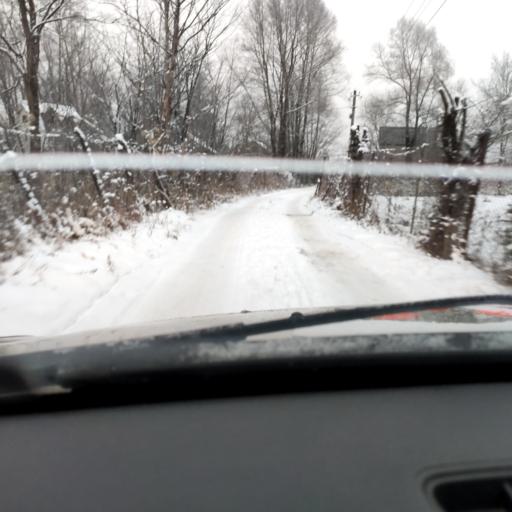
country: RU
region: Bashkortostan
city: Ufa
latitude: 54.6948
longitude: 55.8925
